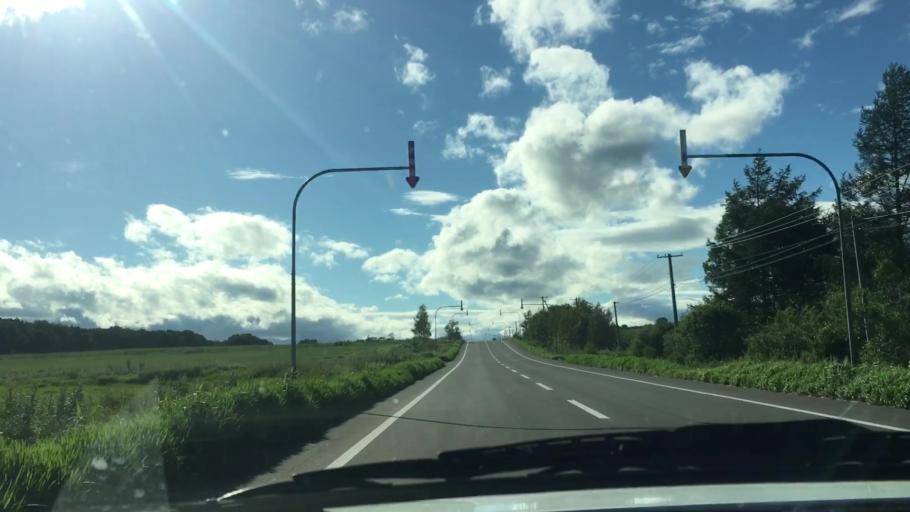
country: JP
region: Hokkaido
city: Otofuke
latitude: 43.1640
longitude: 143.1448
